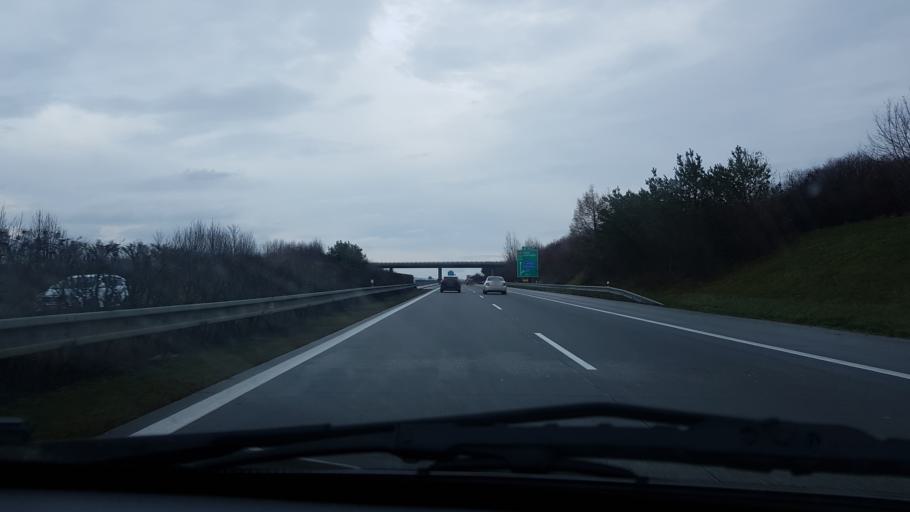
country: CZ
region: Olomoucky
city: Praslavice
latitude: 49.5767
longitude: 17.3750
